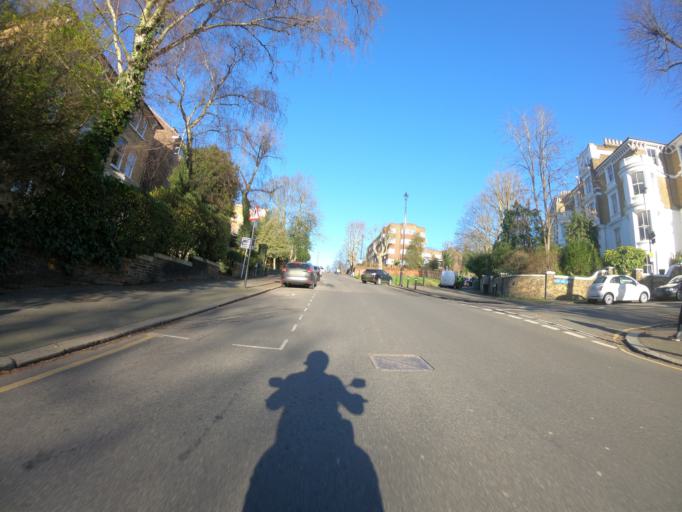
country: GB
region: England
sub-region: Greater London
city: Blackheath
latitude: 51.4675
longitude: -0.0092
